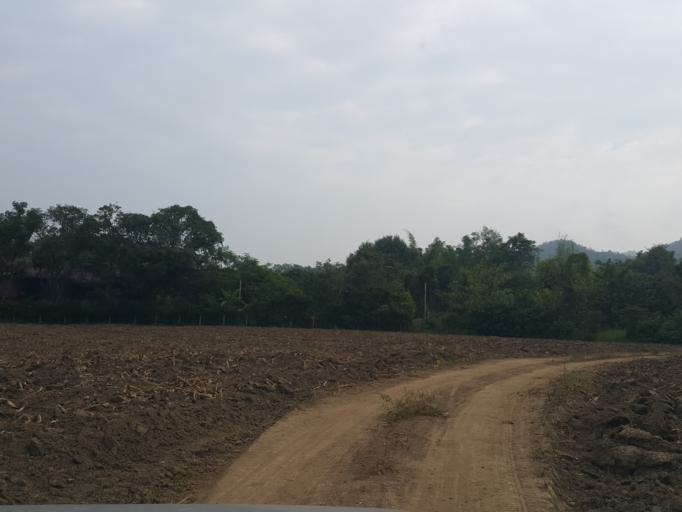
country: TH
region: Chiang Mai
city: Pai
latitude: 19.3652
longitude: 98.4461
